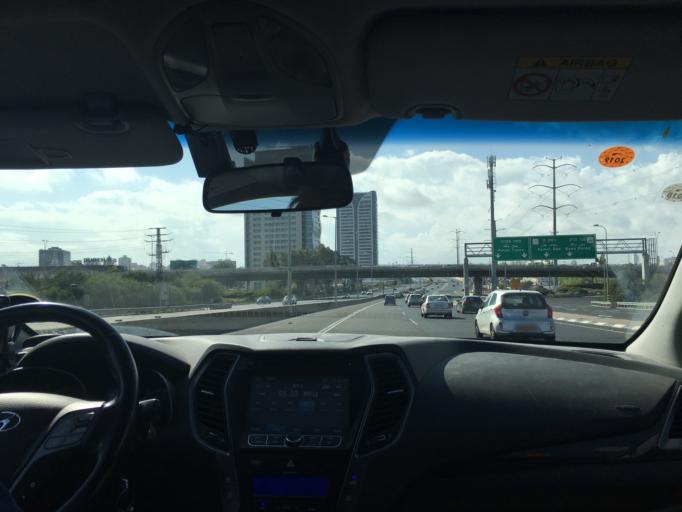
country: IL
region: Tel Aviv
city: Giv`at Shemu'el
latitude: 32.1020
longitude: 34.8481
